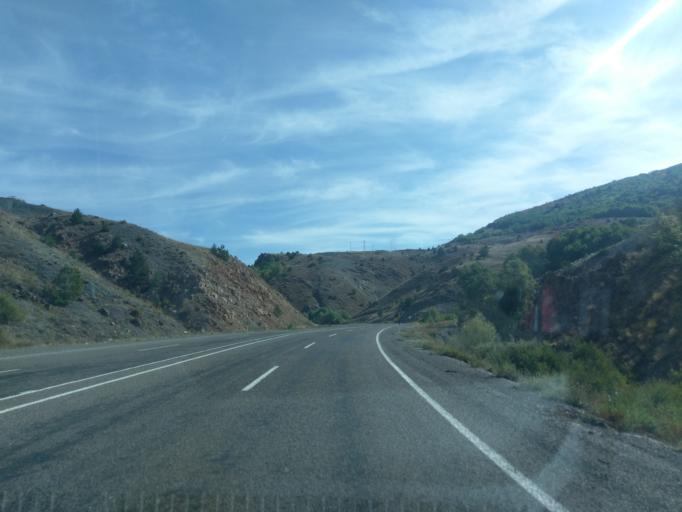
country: TR
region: Sivas
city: Imranli
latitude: 39.8573
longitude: 38.3129
